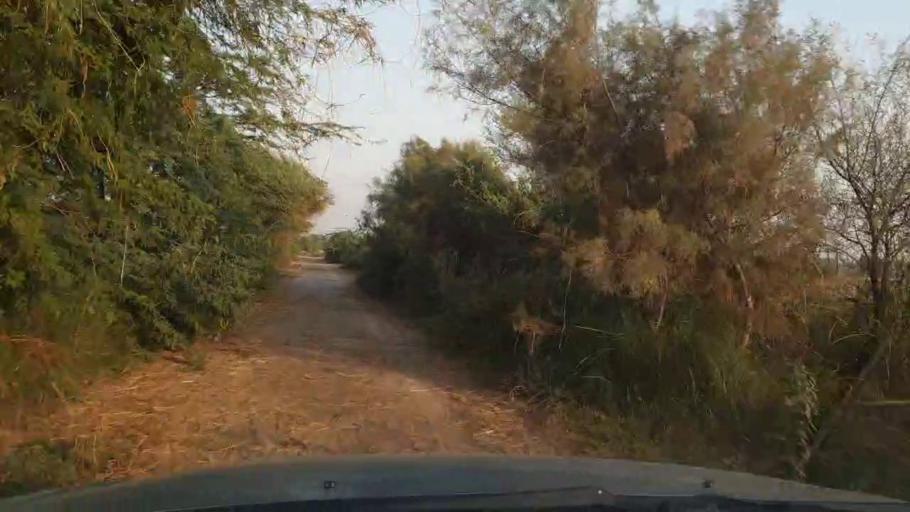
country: PK
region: Sindh
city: Tando Muhammad Khan
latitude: 24.9971
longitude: 68.4337
